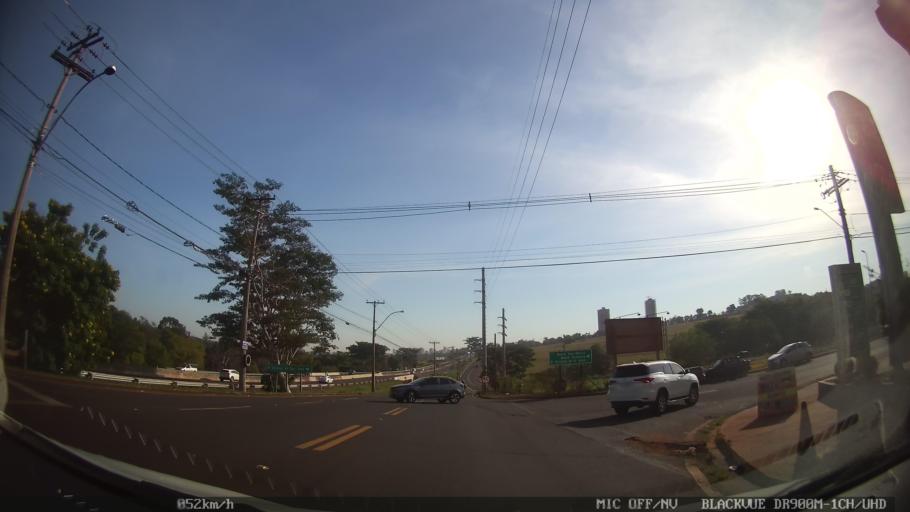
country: BR
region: Sao Paulo
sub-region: Ribeirao Preto
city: Ribeirao Preto
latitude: -21.2500
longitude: -47.8191
